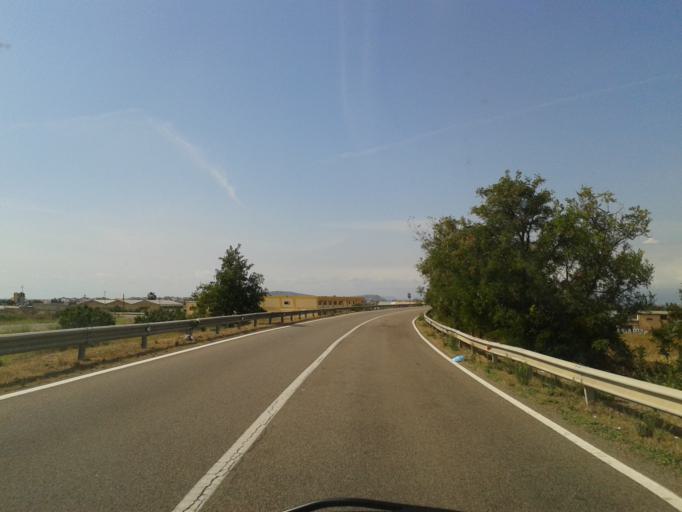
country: IT
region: Sardinia
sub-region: Provincia di Cagliari
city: Quartucciu
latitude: 39.2575
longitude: 9.1939
